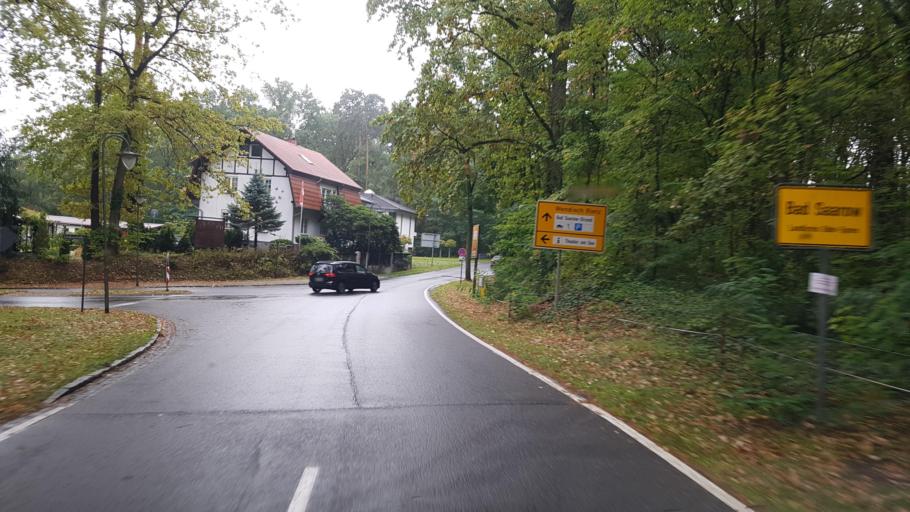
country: DE
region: Brandenburg
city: Bad Saarow
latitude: 52.2945
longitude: 14.0461
